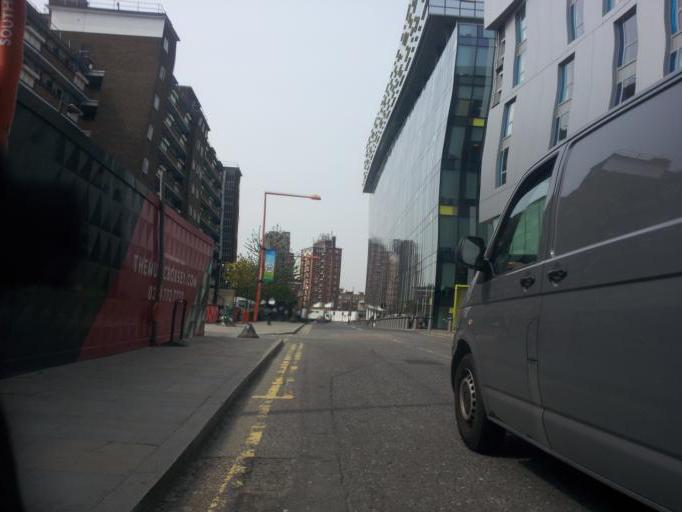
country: GB
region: England
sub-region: Greater London
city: Lambeth
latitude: 51.5036
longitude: -0.1023
